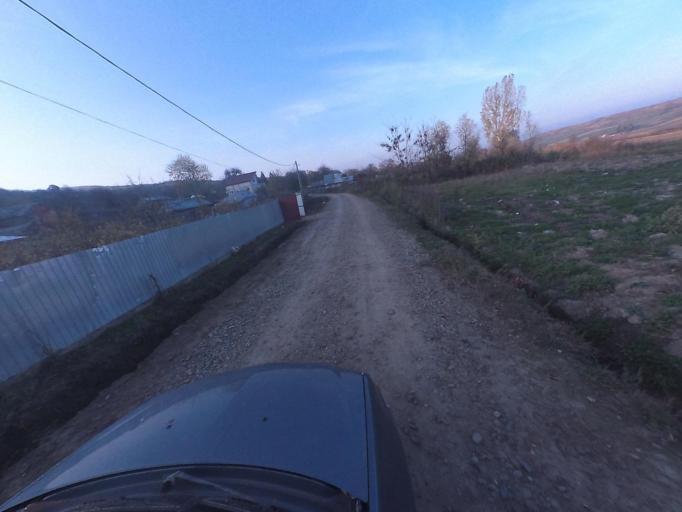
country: RO
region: Vaslui
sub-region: Comuna Bacesti
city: Bacesti
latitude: 46.7992
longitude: 27.2252
